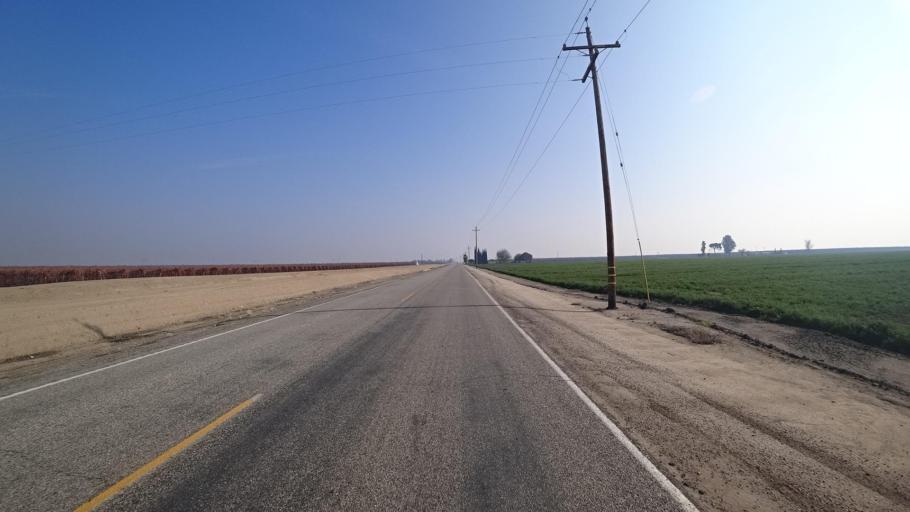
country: US
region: California
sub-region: Kern County
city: Buttonwillow
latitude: 35.3546
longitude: -119.3881
